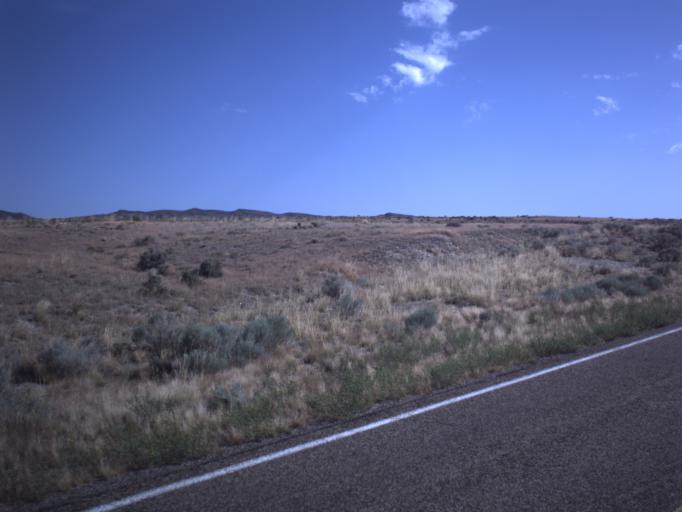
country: US
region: Utah
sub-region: Beaver County
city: Milford
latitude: 38.7720
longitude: -112.9327
